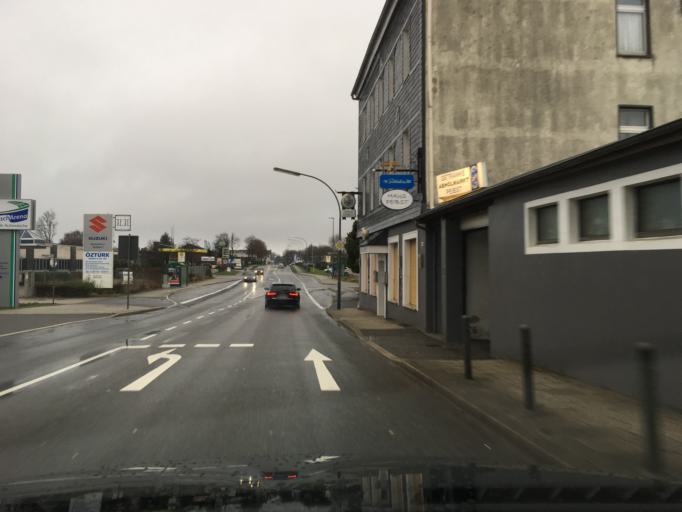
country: DE
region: North Rhine-Westphalia
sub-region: Regierungsbezirk Dusseldorf
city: Velbert
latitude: 51.3175
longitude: 7.0635
